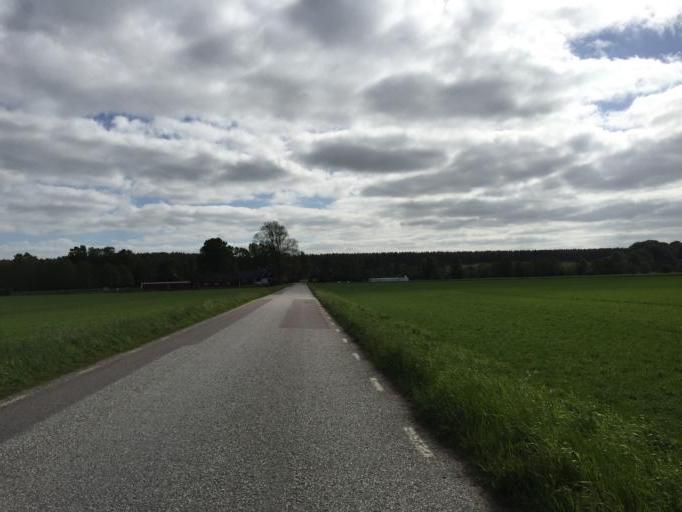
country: SE
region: Skane
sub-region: Sjobo Kommun
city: Blentarp
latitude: 55.6654
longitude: 13.6201
